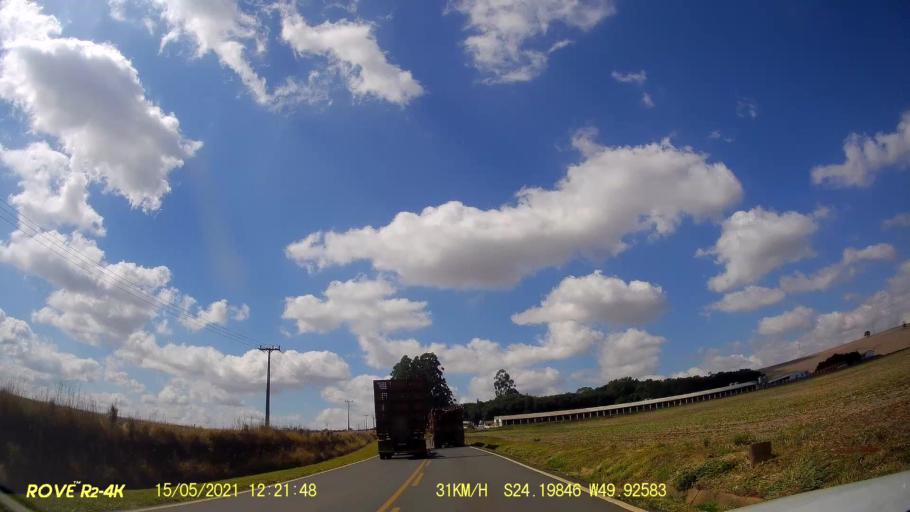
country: BR
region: Parana
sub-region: Jaguariaiva
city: Jaguariaiva
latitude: -24.1984
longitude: -49.9255
